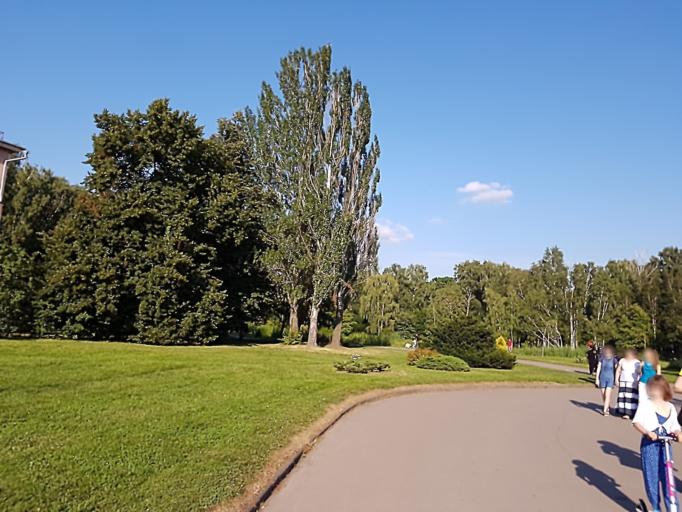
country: RU
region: Moscow
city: Novovladykino
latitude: 55.8438
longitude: 37.5903
